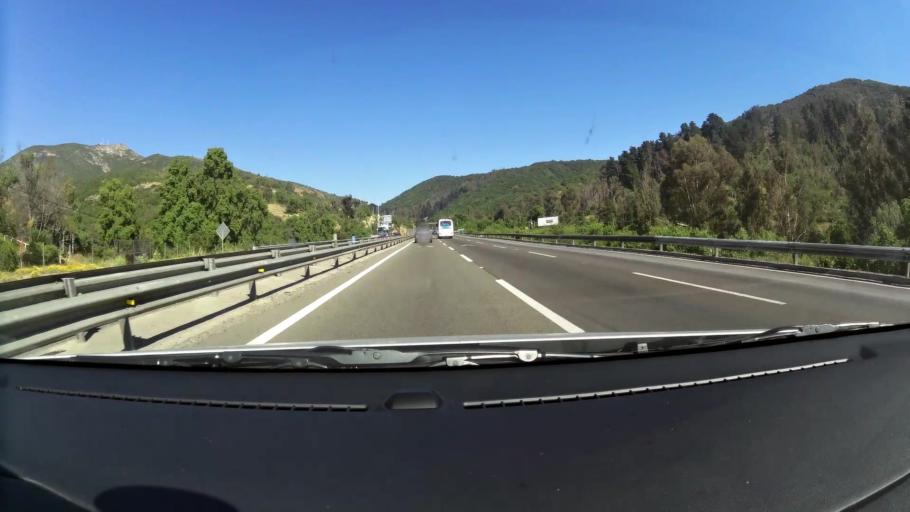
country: CL
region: Santiago Metropolitan
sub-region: Provincia de Melipilla
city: Melipilla
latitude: -33.3934
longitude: -71.2487
